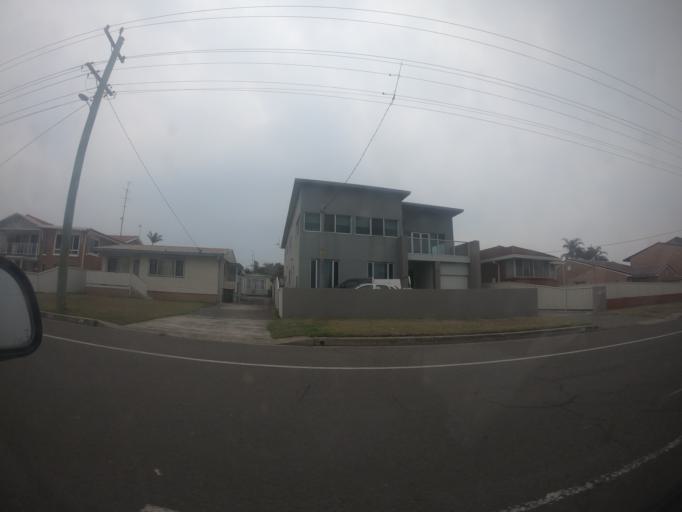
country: AU
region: New South Wales
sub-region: Shellharbour
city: Lake Illawarra
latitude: -34.5500
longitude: 150.8679
